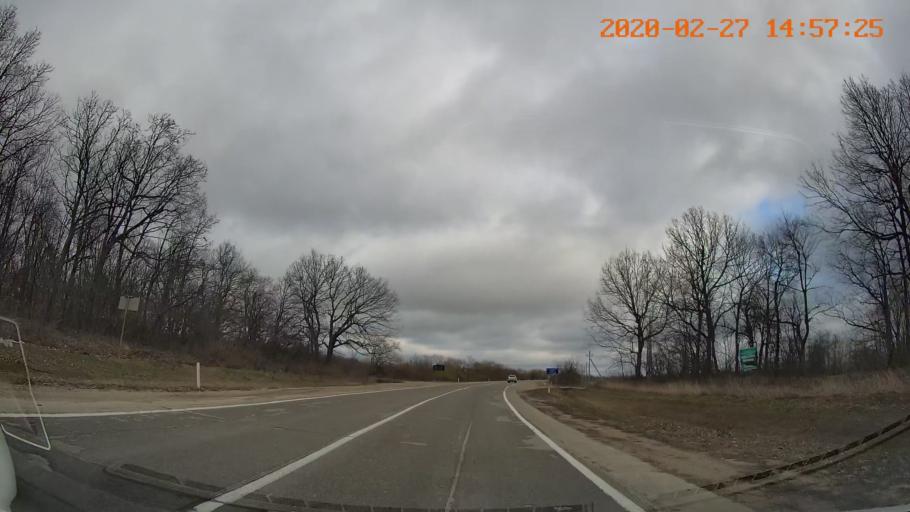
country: MD
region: Chisinau
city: Vatra
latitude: 47.1530
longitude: 28.7573
